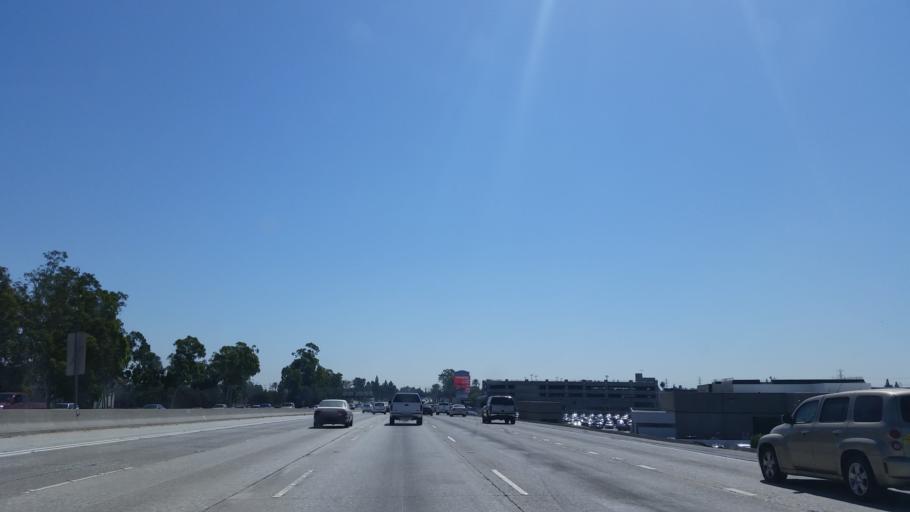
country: US
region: California
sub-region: Los Angeles County
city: Artesia
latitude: 33.8650
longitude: -118.0985
